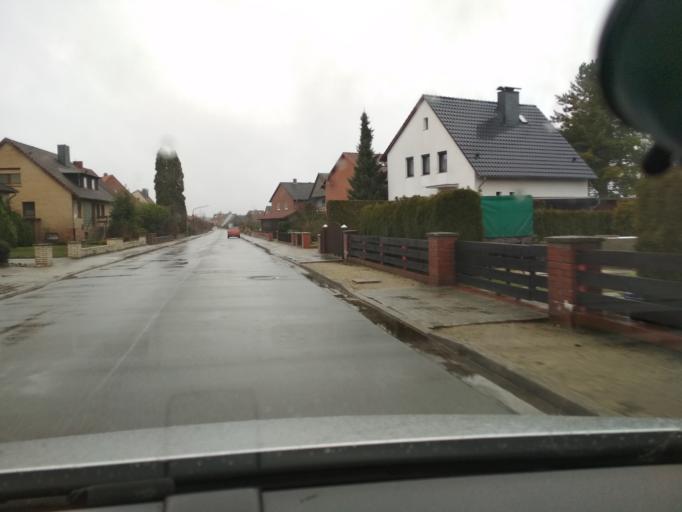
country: DE
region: Lower Saxony
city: Wittingen
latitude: 52.6753
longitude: 10.6986
